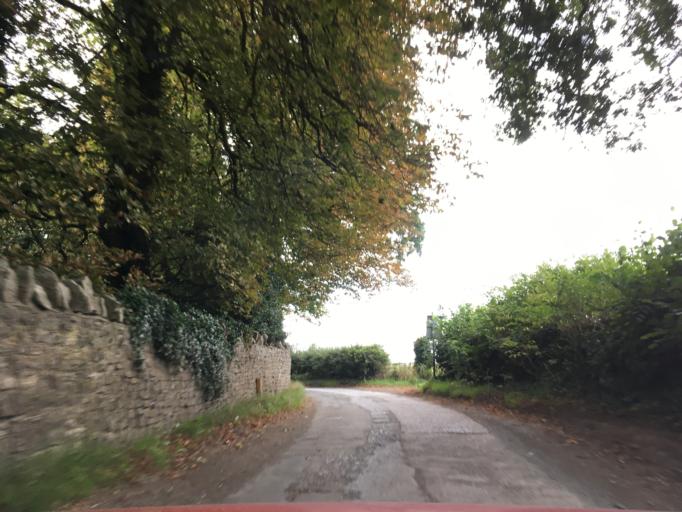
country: GB
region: England
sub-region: South Gloucestershire
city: Alveston
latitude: 51.5864
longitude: -2.5607
